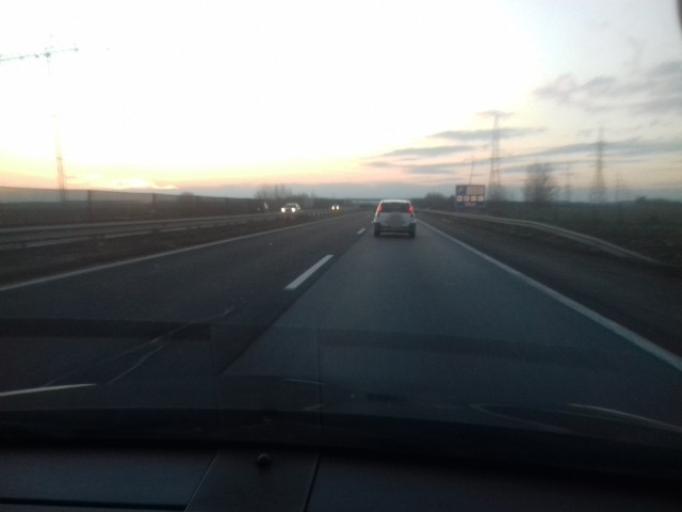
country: HU
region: Hajdu-Bihar
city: Polgar
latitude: 47.8485
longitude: 21.1131
